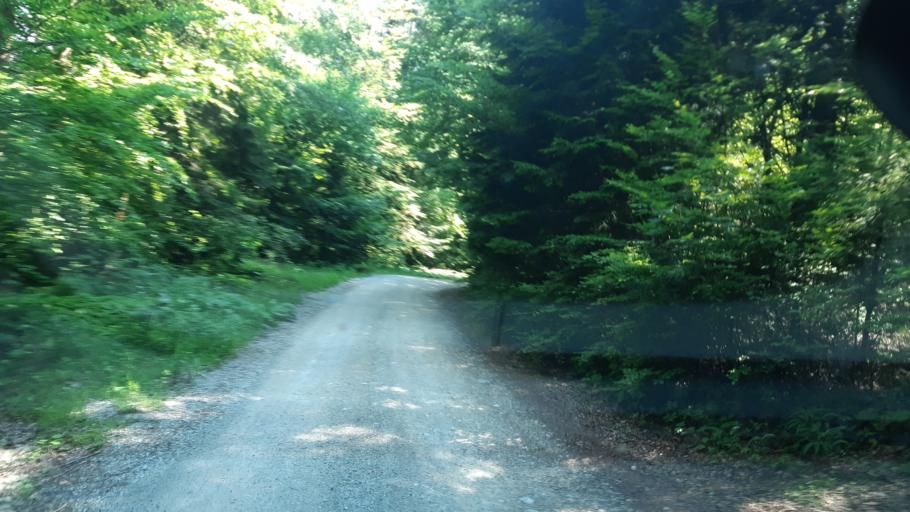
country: SI
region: Trzic
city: Bistrica pri Trzicu
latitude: 46.3751
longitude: 14.2742
